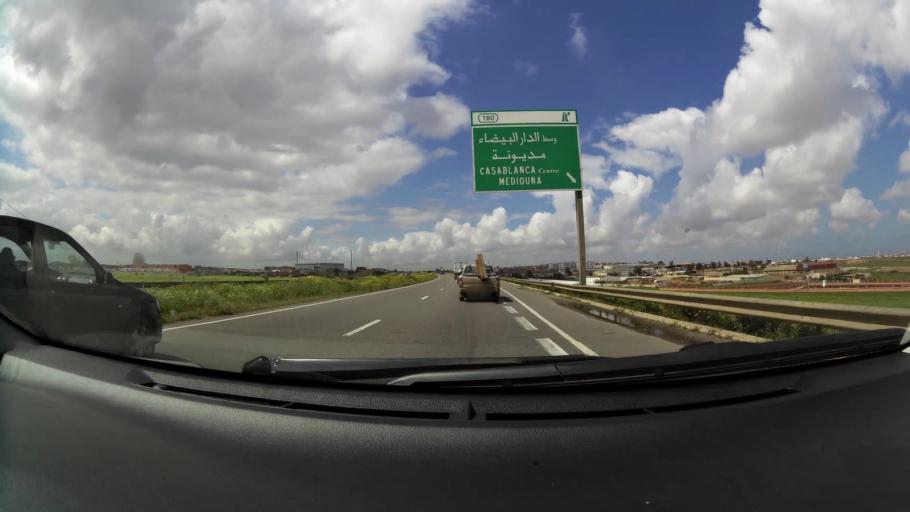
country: MA
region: Grand Casablanca
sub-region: Casablanca
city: Casablanca
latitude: 33.5303
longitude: -7.5617
